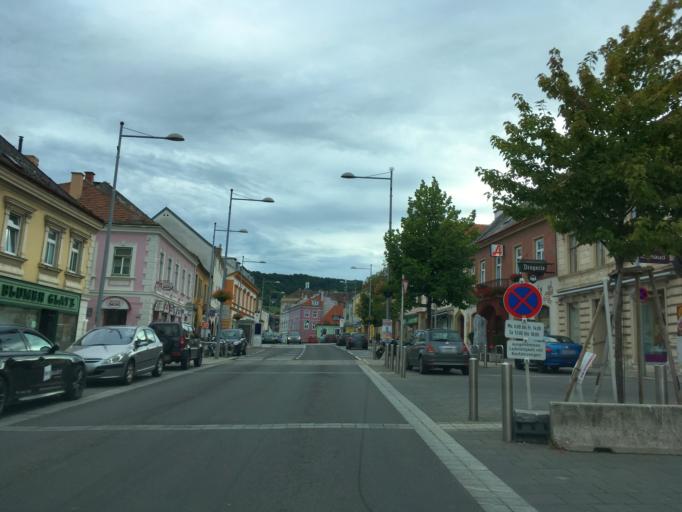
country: AT
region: Lower Austria
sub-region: Politischer Bezirk Wien-Umgebung
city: Klosterneuburg
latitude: 48.3092
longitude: 16.3235
